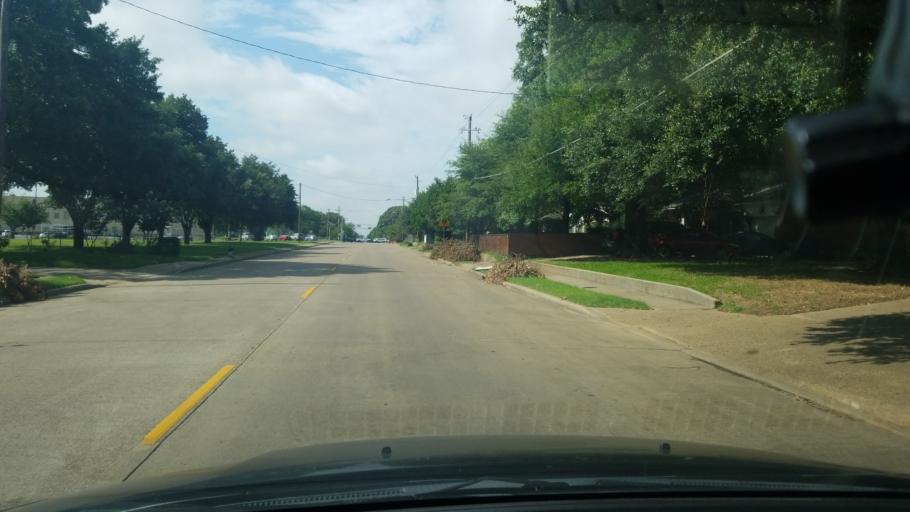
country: US
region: Texas
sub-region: Dallas County
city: Balch Springs
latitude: 32.7514
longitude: -96.6786
